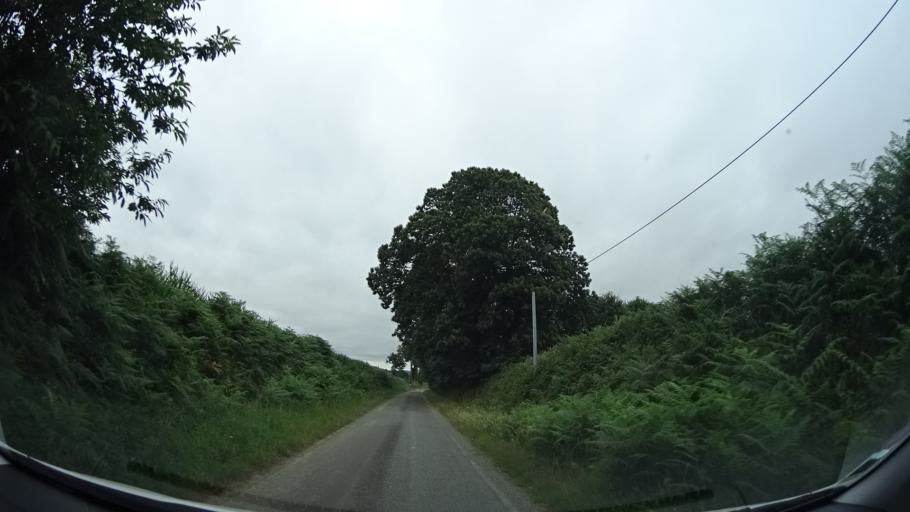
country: FR
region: Brittany
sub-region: Departement des Cotes-d'Armor
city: Evran
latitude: 48.3348
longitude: -1.9489
